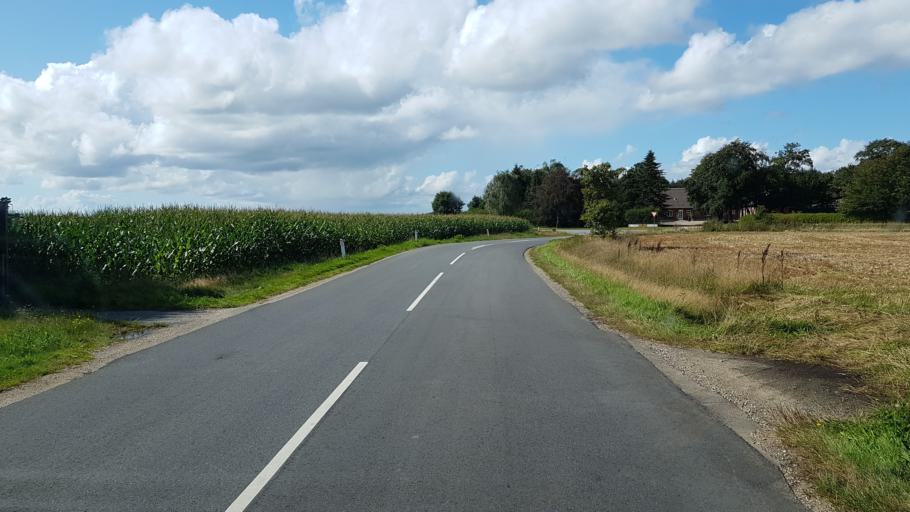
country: DK
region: South Denmark
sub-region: Esbjerg Kommune
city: Bramming
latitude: 55.6149
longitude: 8.7532
